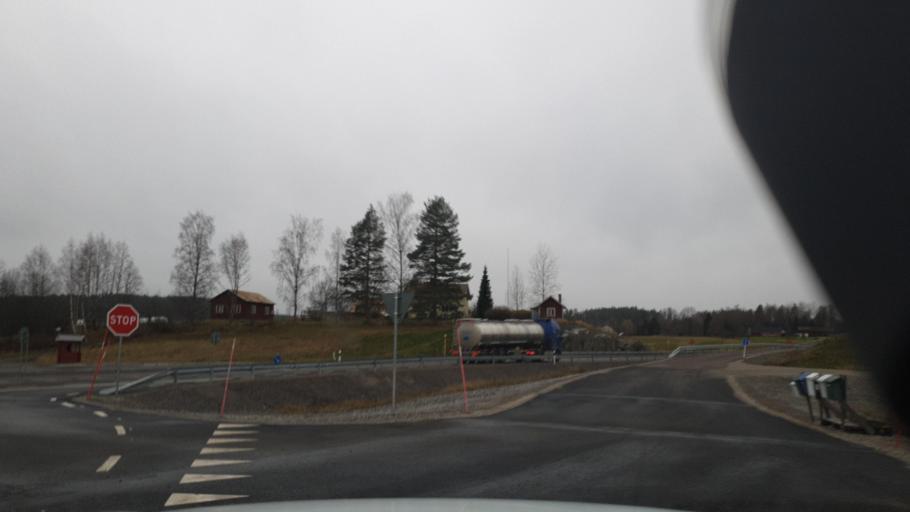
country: SE
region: Vaermland
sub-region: Arvika Kommun
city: Arvika
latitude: 59.7096
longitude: 12.5588
